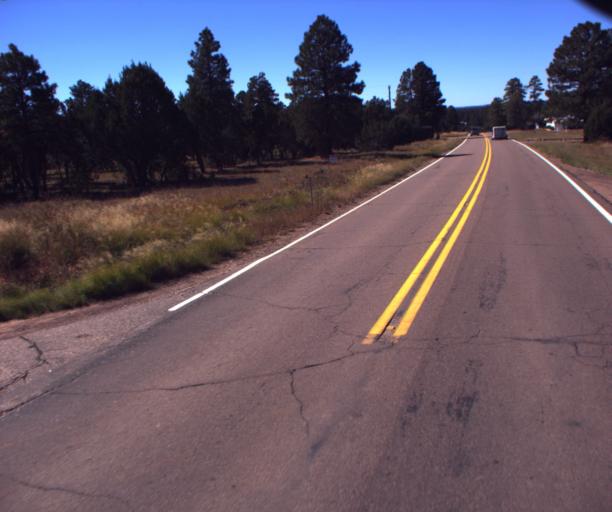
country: US
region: Arizona
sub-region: Navajo County
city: Heber-Overgaard
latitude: 34.4223
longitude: -110.5669
